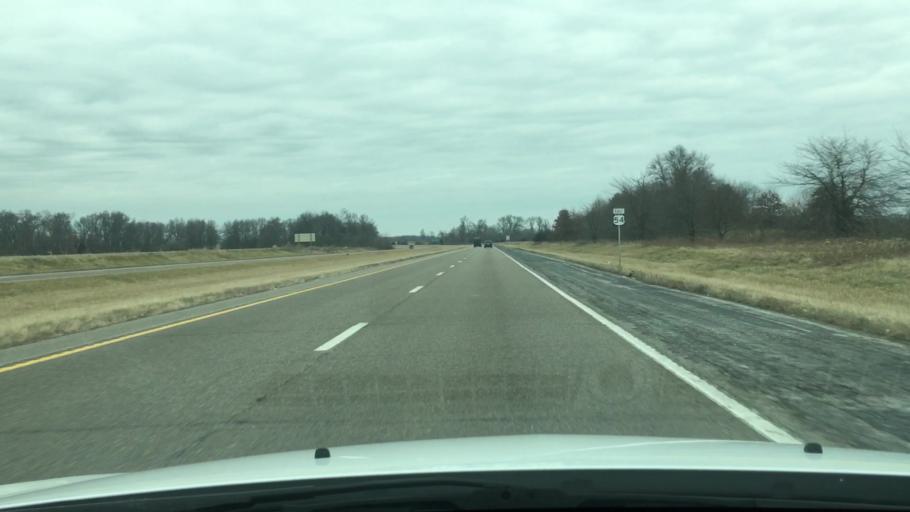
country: US
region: Missouri
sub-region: Audrain County
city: Mexico
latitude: 39.0241
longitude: -91.8856
